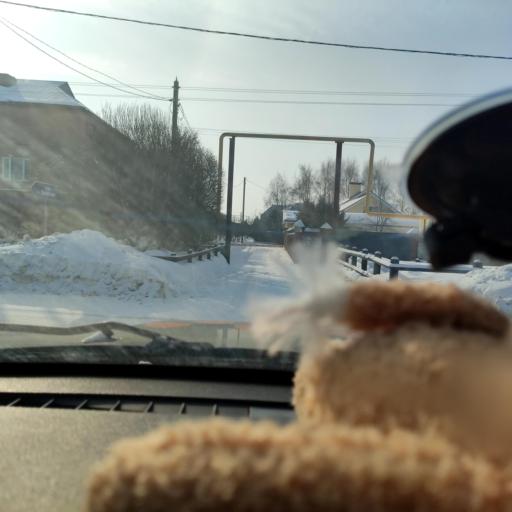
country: RU
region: Samara
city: Podstepki
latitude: 53.5108
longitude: 49.1197
